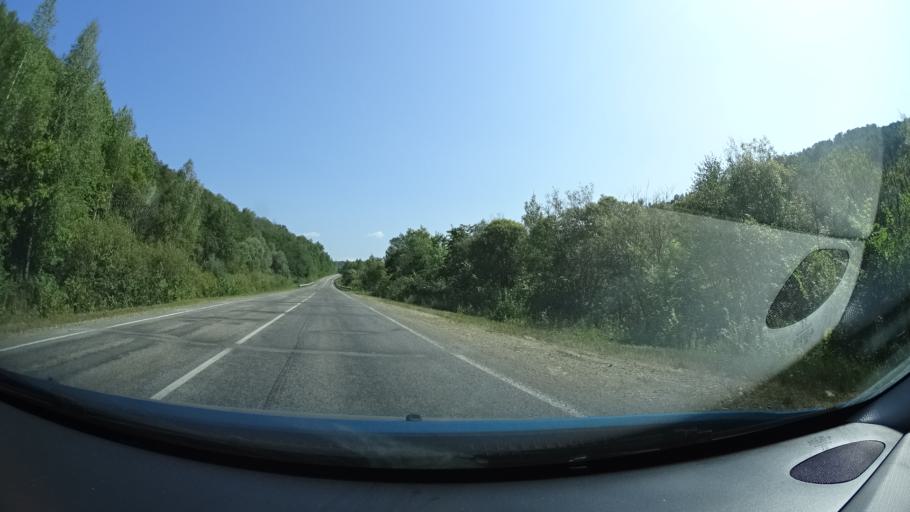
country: RU
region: Bashkortostan
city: Inzer
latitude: 54.3379
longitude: 57.0956
